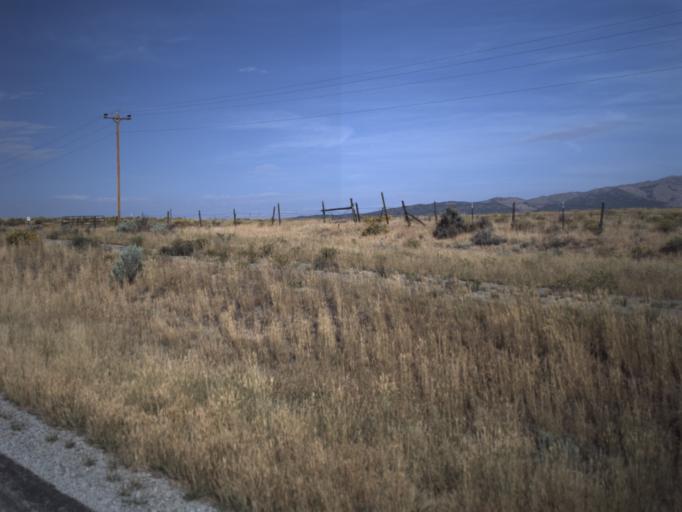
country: US
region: Idaho
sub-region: Oneida County
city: Malad City
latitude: 41.9653
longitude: -113.0555
